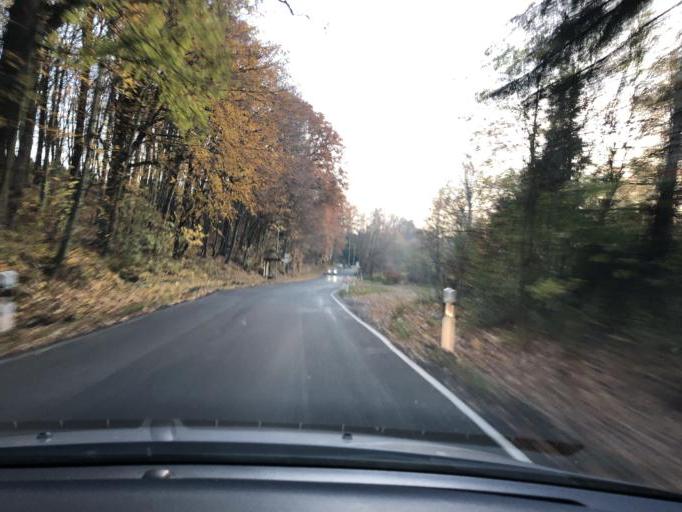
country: DE
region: Saxony
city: Nerchau
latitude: 51.2511
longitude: 12.7764
